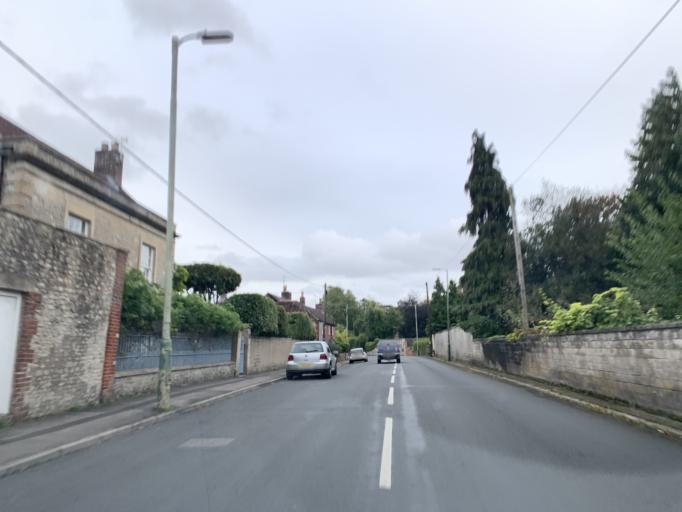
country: GB
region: England
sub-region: Wiltshire
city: Bishopstrow
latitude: 51.1969
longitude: -2.1547
